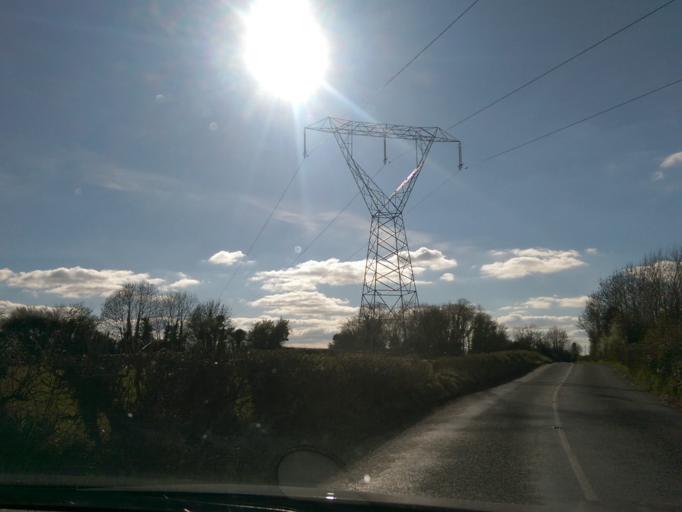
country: IE
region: Leinster
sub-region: Uibh Fhaili
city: Banagher
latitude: 53.1063
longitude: -8.0457
